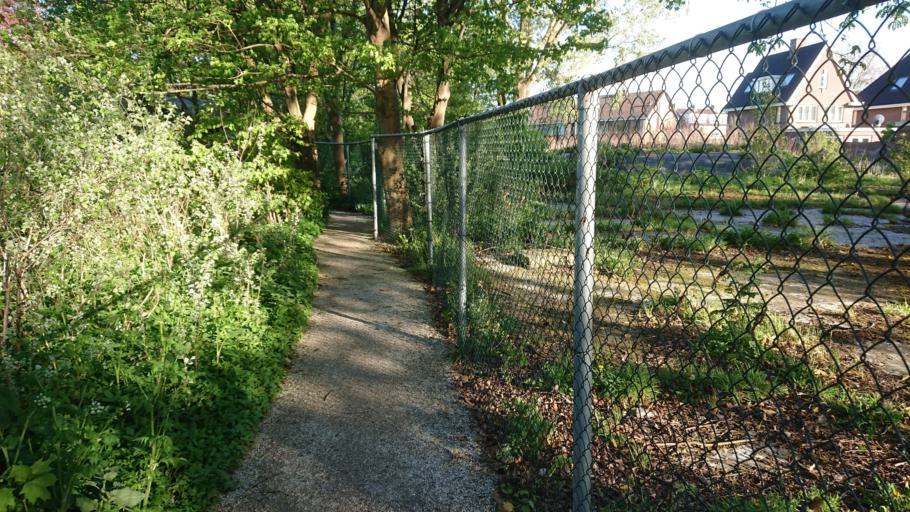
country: NL
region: South Holland
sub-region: Gemeente Teylingen
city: Voorhout
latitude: 52.2203
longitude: 4.4834
